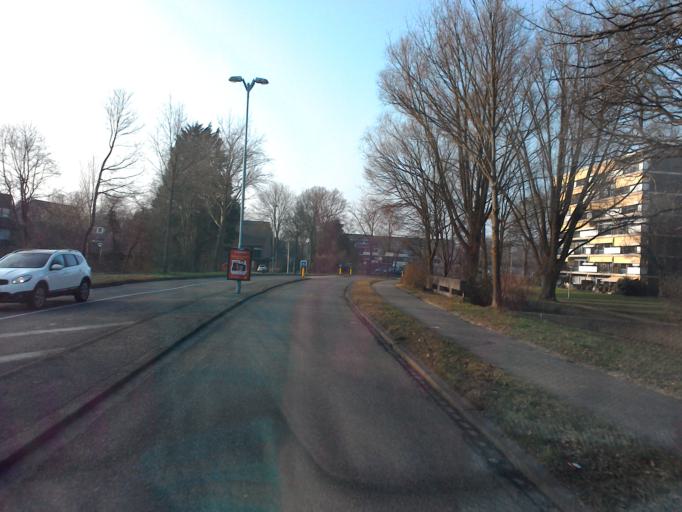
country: NL
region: Utrecht
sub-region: Gemeente Zeist
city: Zeist
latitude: 52.0807
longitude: 5.2179
